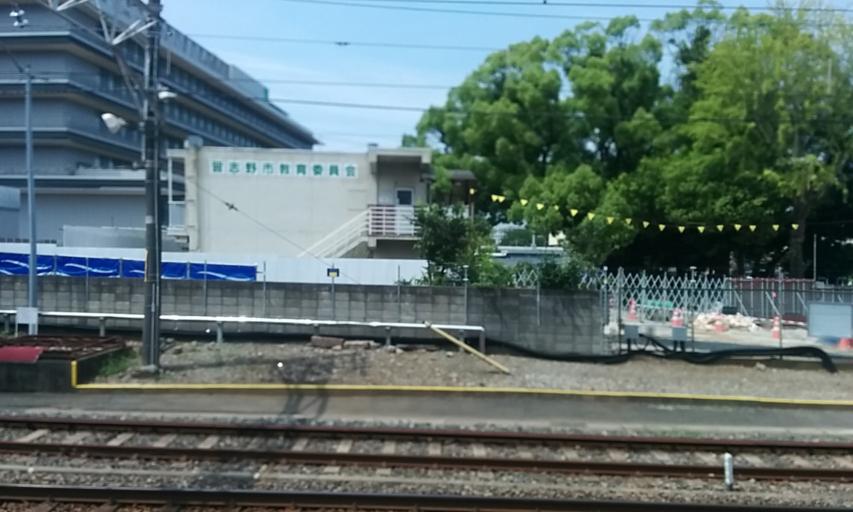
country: JP
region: Chiba
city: Funabashi
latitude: 35.6826
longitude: 140.0276
